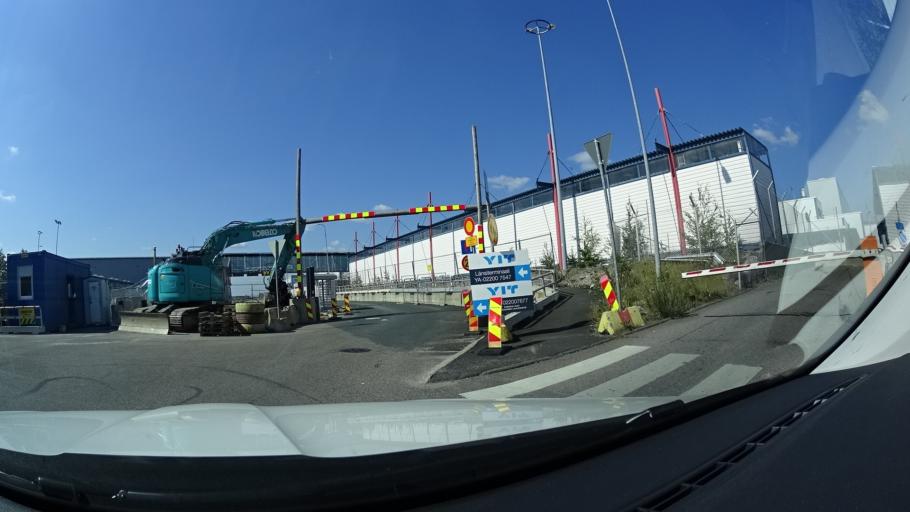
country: FI
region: Uusimaa
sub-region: Helsinki
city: Vantaa
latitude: 60.3090
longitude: 24.9602
